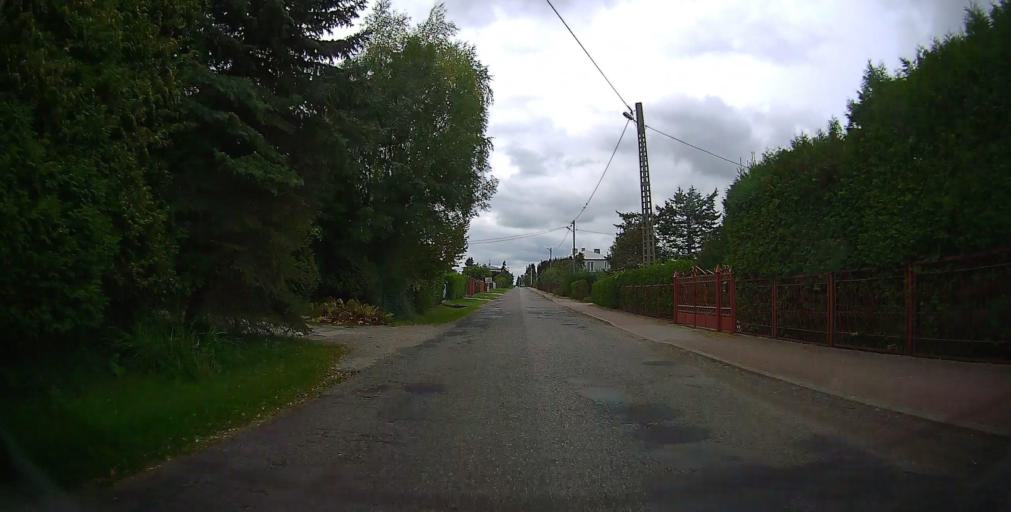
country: PL
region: Masovian Voivodeship
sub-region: Powiat grojecki
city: Belsk Duzy
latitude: 51.8223
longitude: 20.8158
